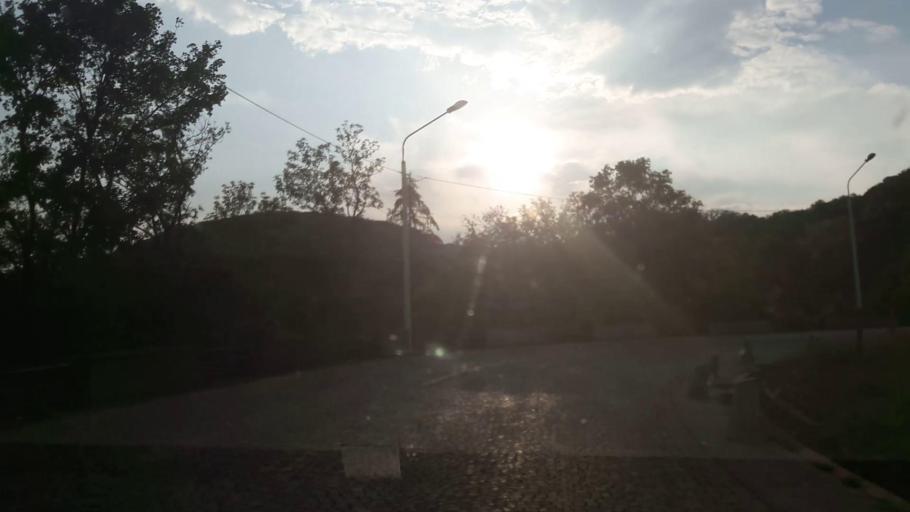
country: AT
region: Lower Austria
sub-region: Politischer Bezirk Wien-Umgebung
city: Klosterneuburg
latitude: 48.2692
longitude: 16.3254
